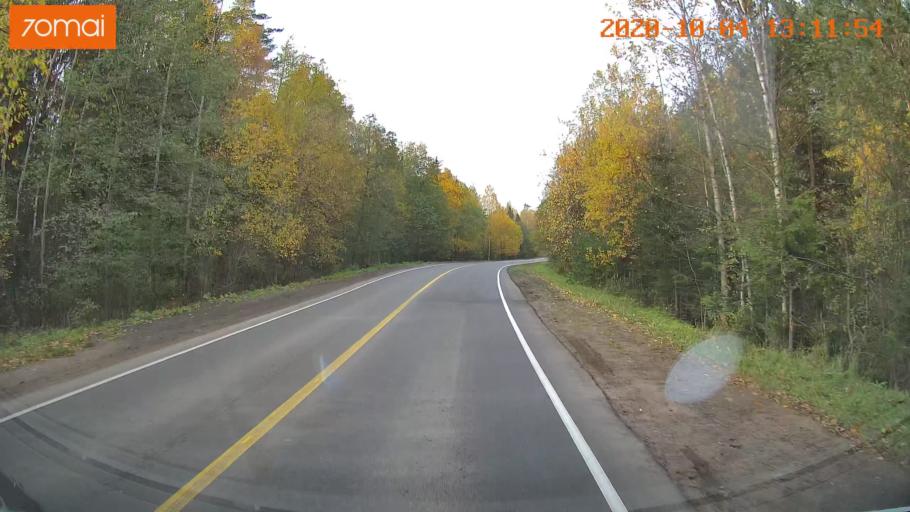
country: RU
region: Ivanovo
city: Bogorodskoye
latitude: 57.0798
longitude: 40.9358
